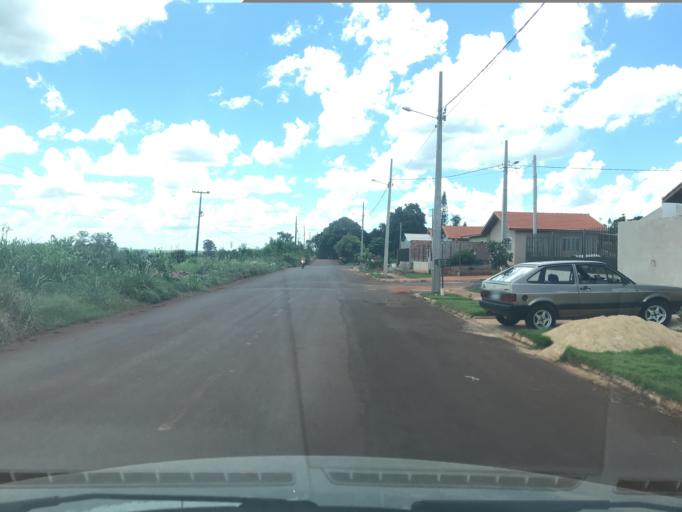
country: BR
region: Parana
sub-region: Palotina
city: Palotina
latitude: -24.2657
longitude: -53.8485
